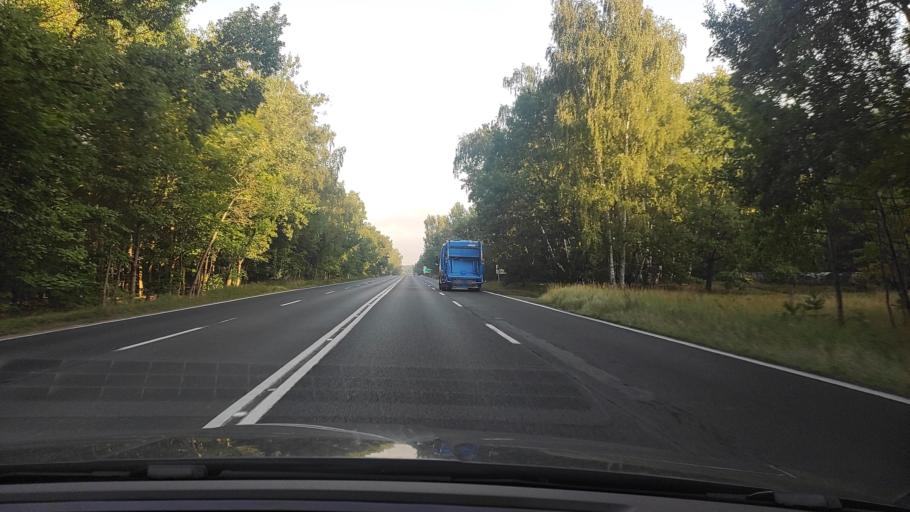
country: PL
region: Greater Poland Voivodeship
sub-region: Powiat poznanski
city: Czerwonak
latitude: 52.4243
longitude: 17.0150
